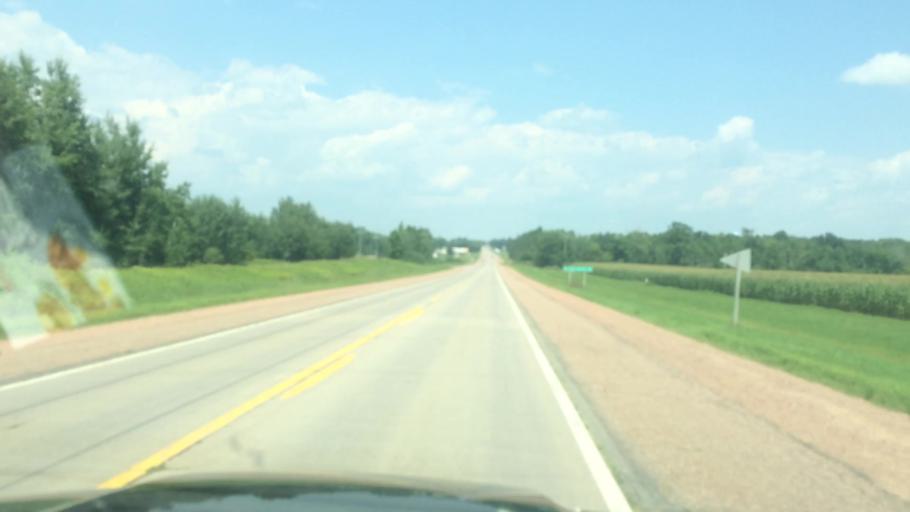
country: US
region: Wisconsin
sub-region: Clark County
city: Colby
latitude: 44.8852
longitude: -90.3154
